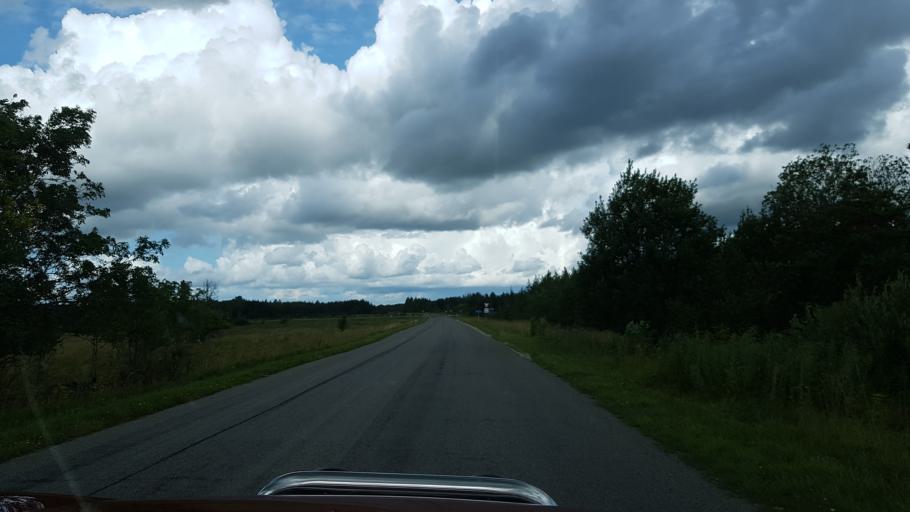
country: EE
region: Laeaene
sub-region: Lihula vald
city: Lihula
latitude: 58.6952
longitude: 23.8306
